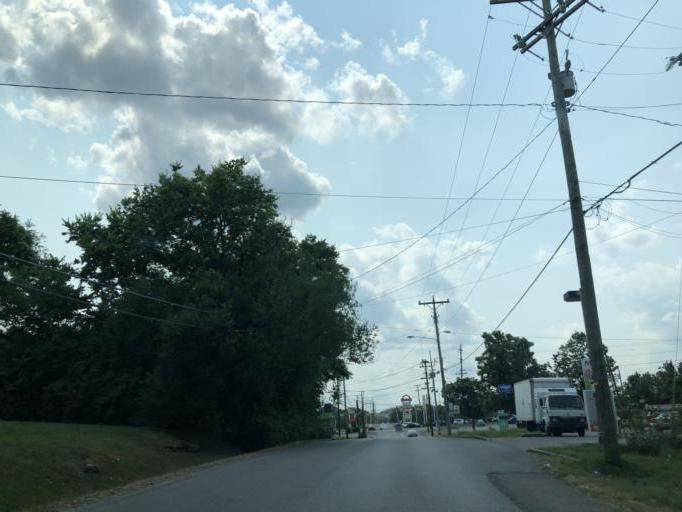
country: US
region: Tennessee
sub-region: Davidson County
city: Goodlettsville
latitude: 36.2479
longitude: -86.7183
